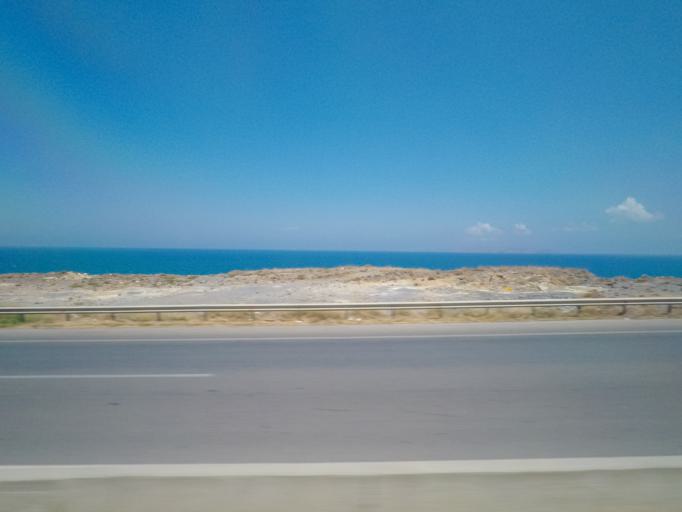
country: GR
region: Crete
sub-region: Nomos Irakleiou
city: Kokkini Hani
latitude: 35.3329
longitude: 25.2204
